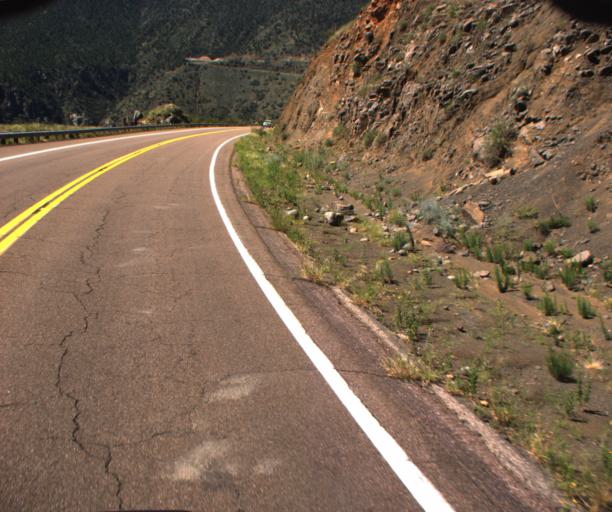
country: US
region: Arizona
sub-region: Navajo County
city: Cibecue
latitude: 33.8008
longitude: -110.4865
